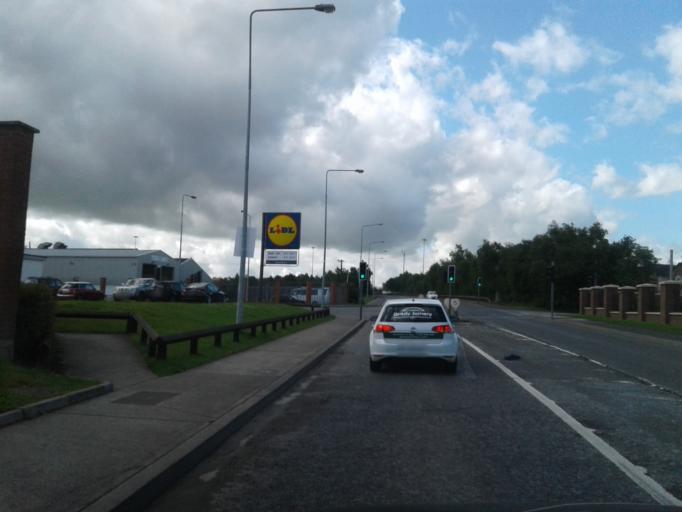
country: IE
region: Leinster
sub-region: Kildare
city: Maynooth
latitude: 53.3700
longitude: -6.5907
